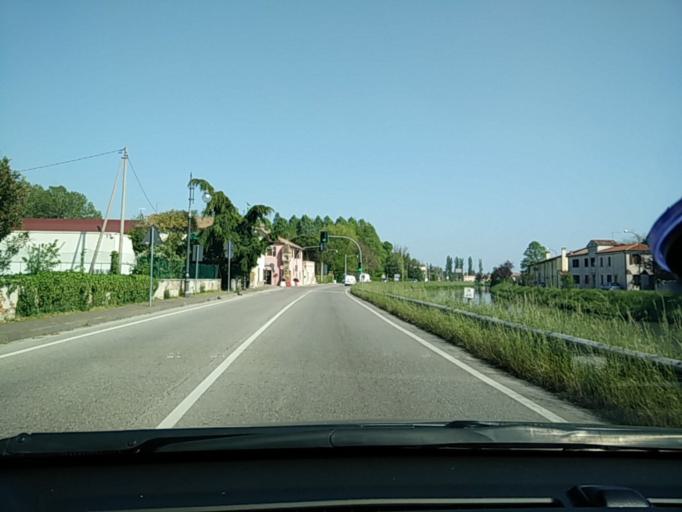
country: IT
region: Veneto
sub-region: Provincia di Venezia
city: Fornase
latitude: 45.4534
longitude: 12.1783
